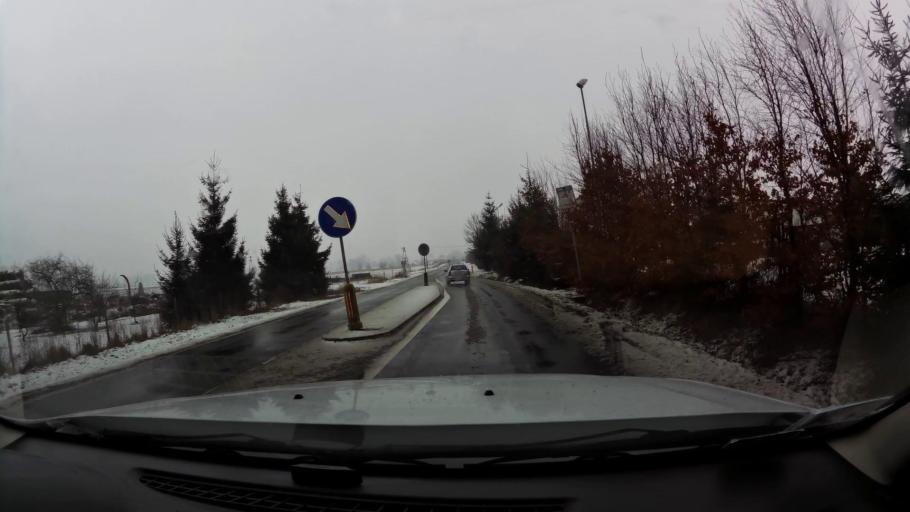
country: PL
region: West Pomeranian Voivodeship
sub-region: Powiat gryficki
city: Trzebiatow
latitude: 54.0991
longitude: 15.2655
